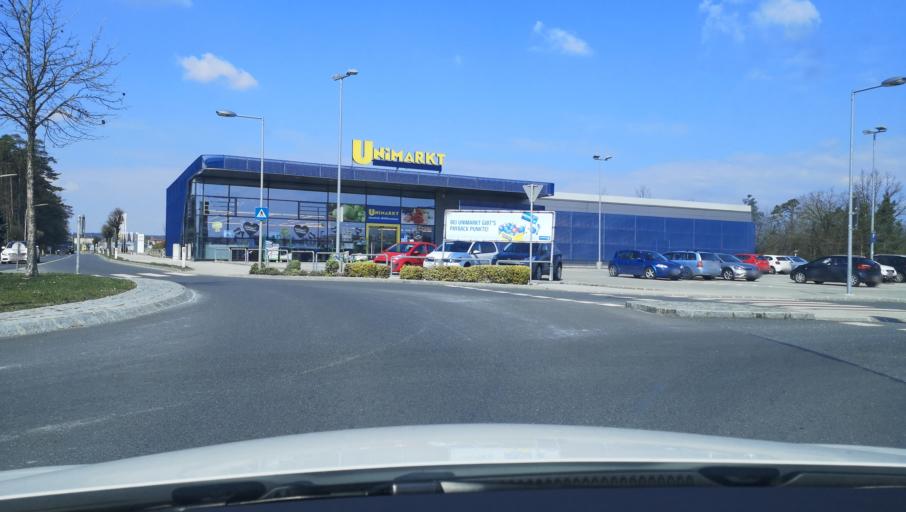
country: AT
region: Lower Austria
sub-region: Politischer Bezirk Amstetten
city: Winklarn
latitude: 48.0803
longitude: 14.8107
